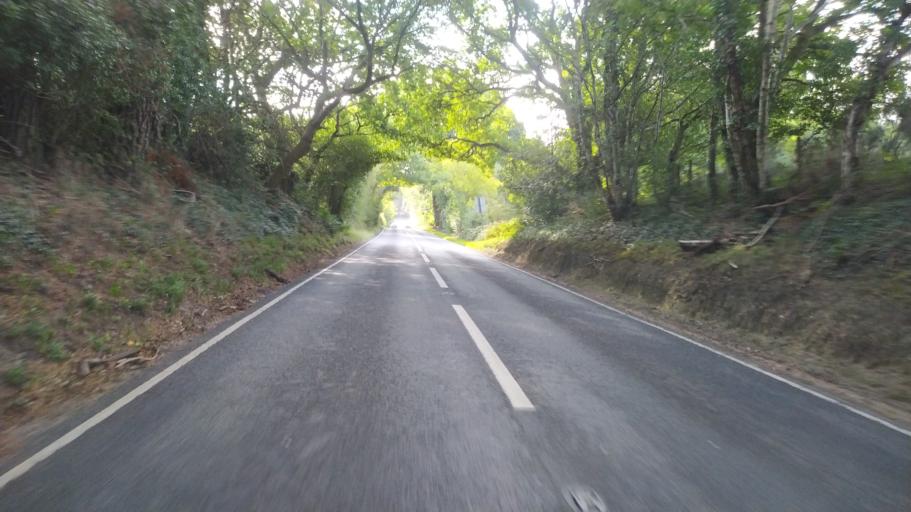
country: GB
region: England
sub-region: Dorset
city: Lytchett Matravers
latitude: 50.7577
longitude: -2.0515
